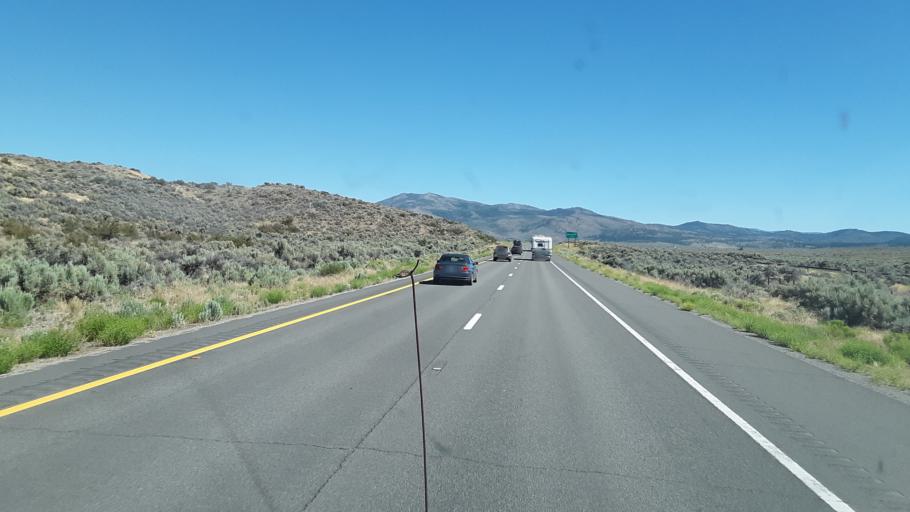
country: US
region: Nevada
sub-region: Washoe County
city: Cold Springs
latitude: 39.6869
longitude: -120.0135
